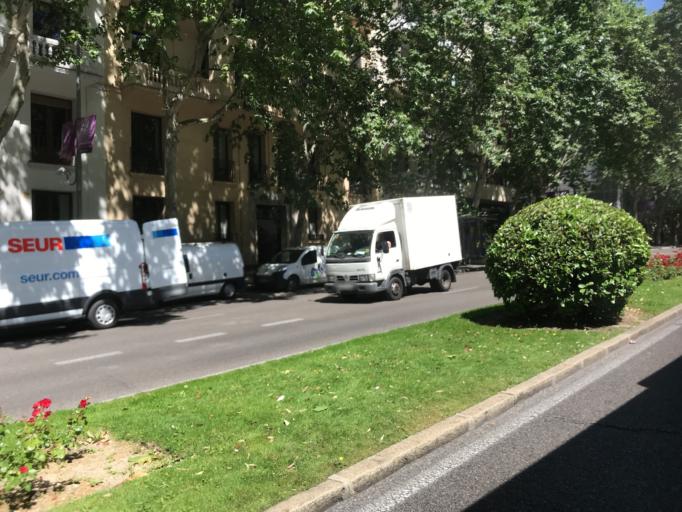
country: ES
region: Madrid
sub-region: Provincia de Madrid
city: Retiro
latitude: 40.4122
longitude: -3.6887
